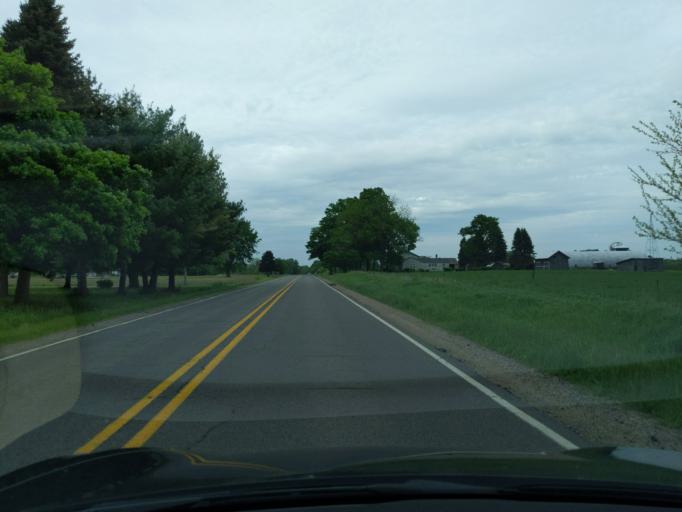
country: US
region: Michigan
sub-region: Ingham County
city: Leslie
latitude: 42.4918
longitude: -84.3562
